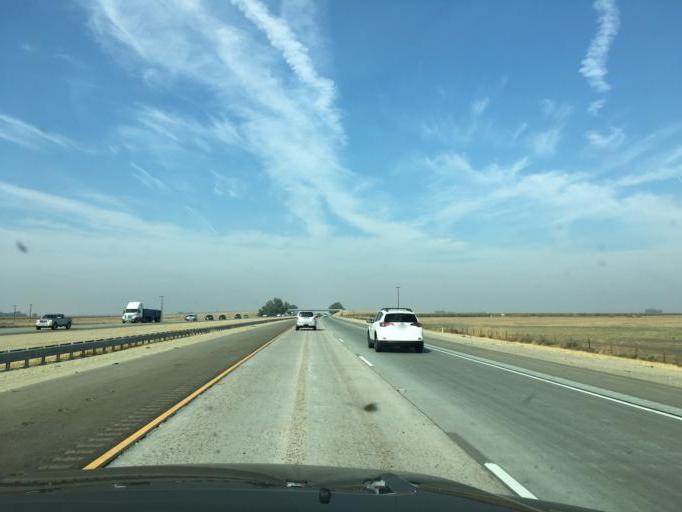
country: US
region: California
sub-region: Kern County
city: Lost Hills
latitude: 35.5706
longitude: -119.6115
